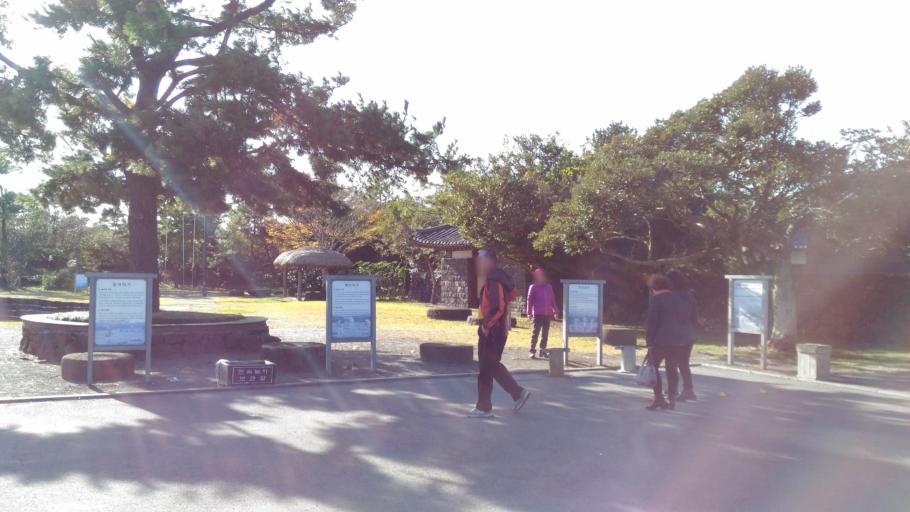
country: KR
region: Jeju-do
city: Seogwipo
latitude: 33.3221
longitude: 126.8425
